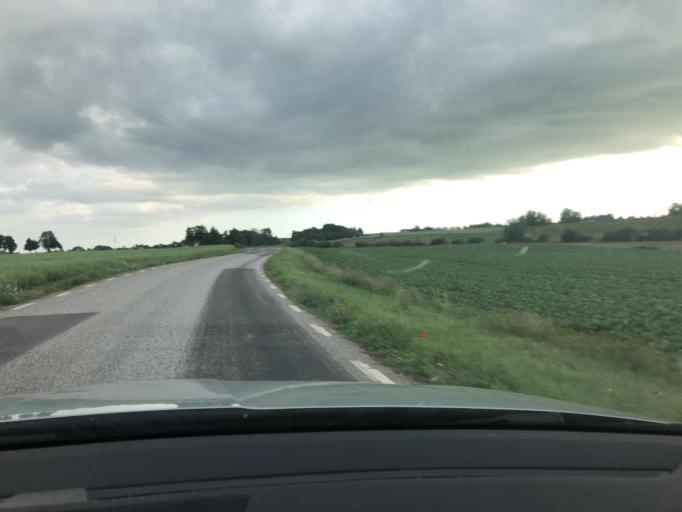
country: SE
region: Skane
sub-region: Simrishamns Kommun
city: Simrishamn
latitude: 55.5051
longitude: 14.2251
